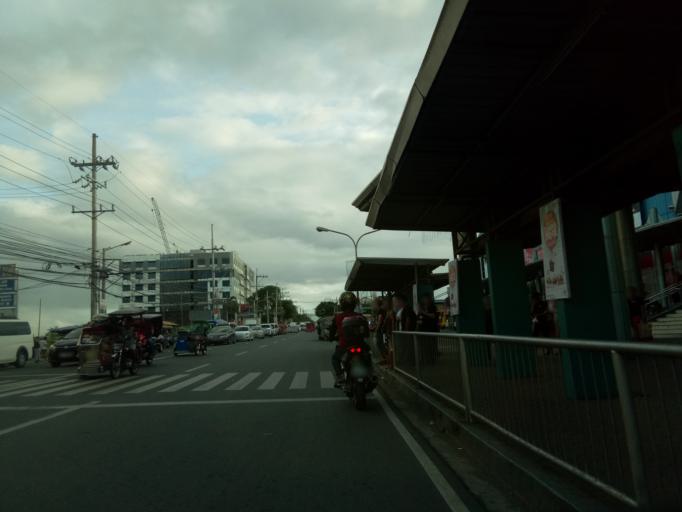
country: PH
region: Calabarzon
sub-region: Province of Cavite
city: Imus
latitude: 14.3846
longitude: 120.9780
